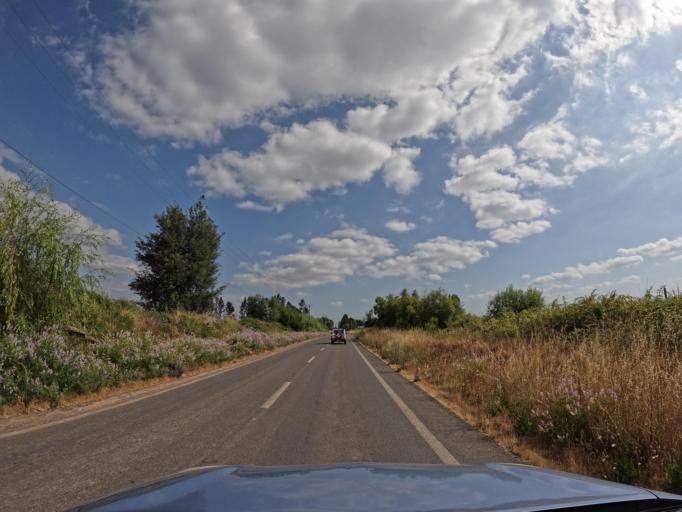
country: CL
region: Maule
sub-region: Provincia de Curico
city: Molina
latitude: -35.1968
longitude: -71.2974
